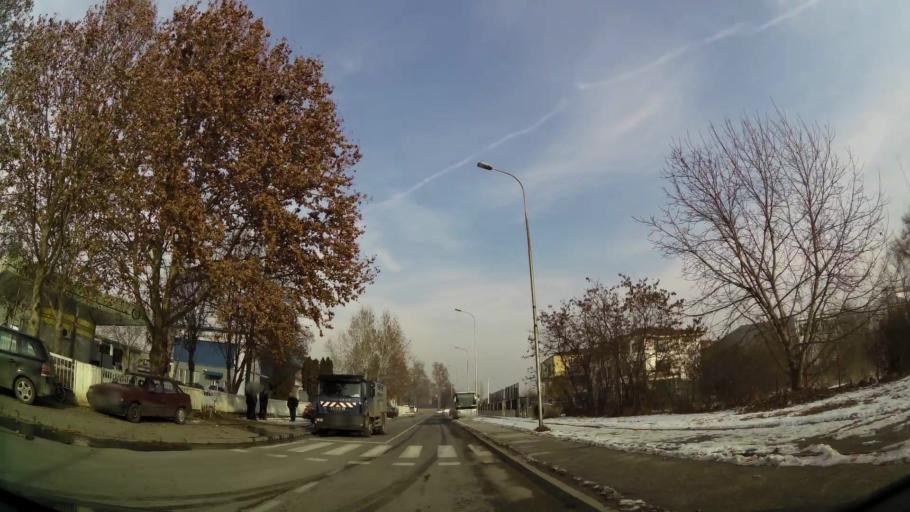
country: MK
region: Cair
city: Cair
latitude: 42.0235
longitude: 21.4341
